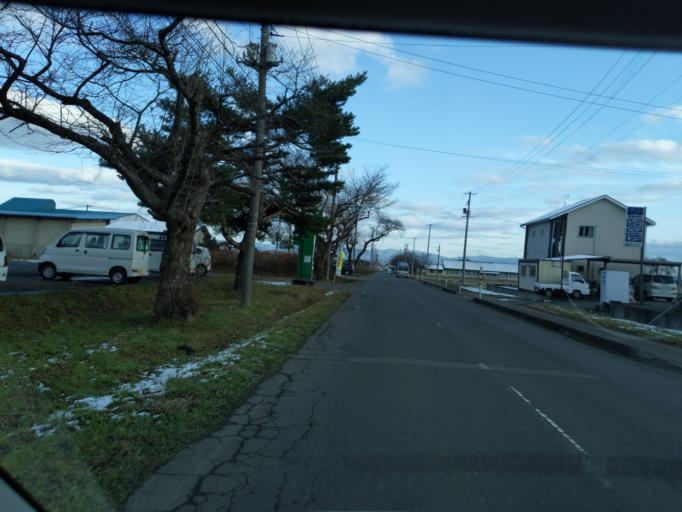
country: JP
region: Iwate
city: Kitakami
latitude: 39.2049
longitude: 141.0490
